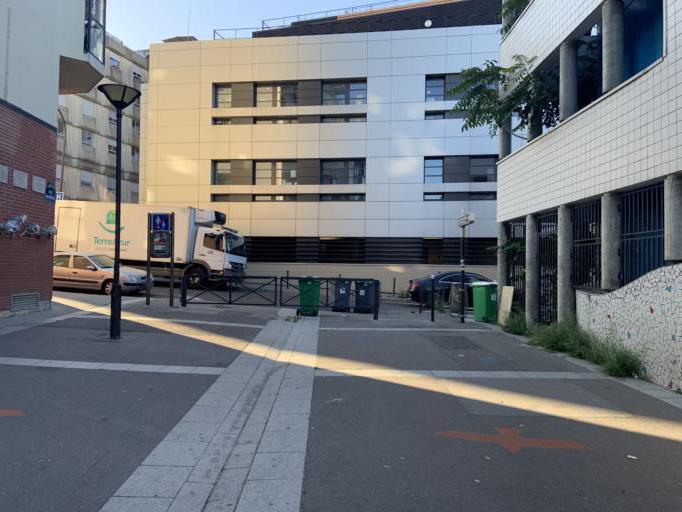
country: FR
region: Ile-de-France
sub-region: Departement de Seine-Saint-Denis
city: Bagnolet
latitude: 48.8546
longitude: 2.4080
